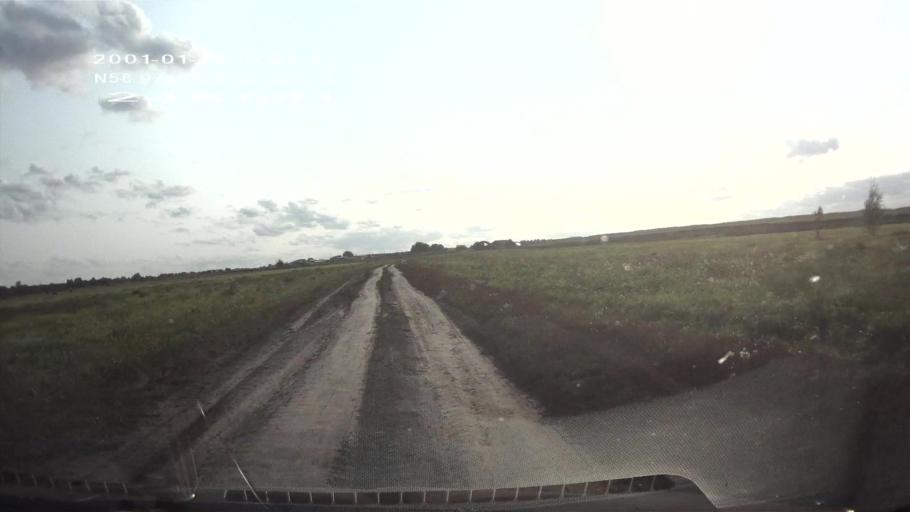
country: RU
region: Mariy-El
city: Kuzhener
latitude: 56.9743
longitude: 48.7957
